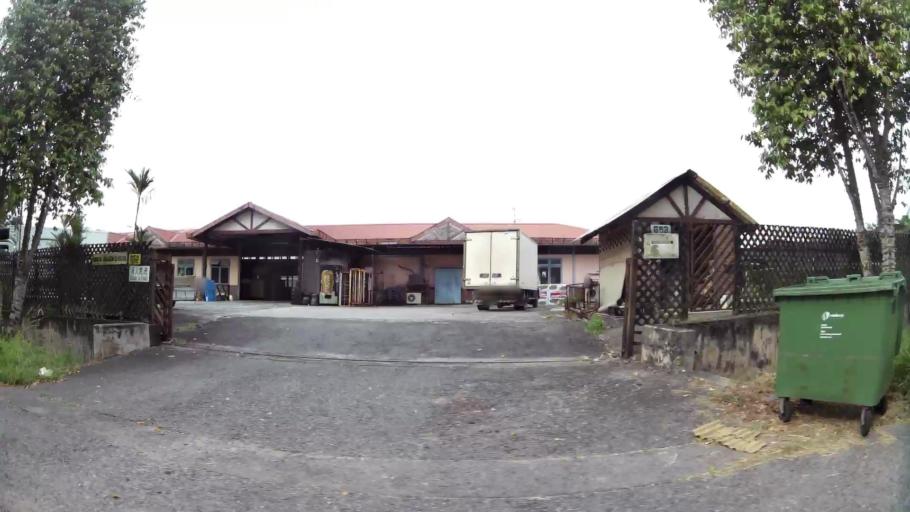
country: MY
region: Johor
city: Johor Bahru
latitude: 1.4422
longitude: 103.7093
